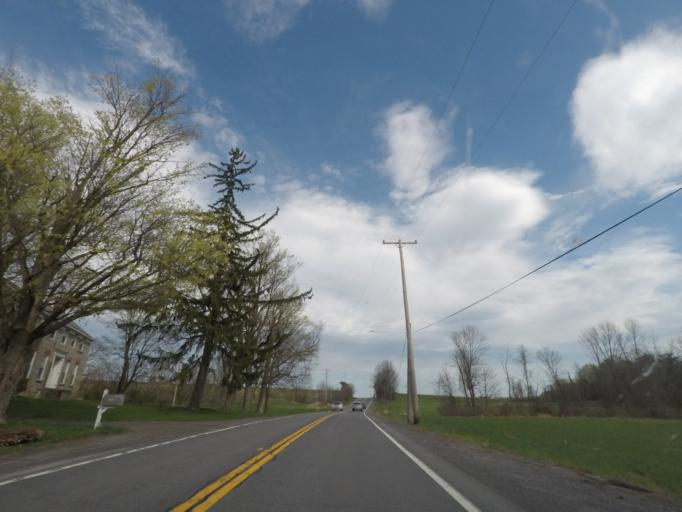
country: US
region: New York
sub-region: Albany County
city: Voorheesville
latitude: 42.5698
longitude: -73.9101
